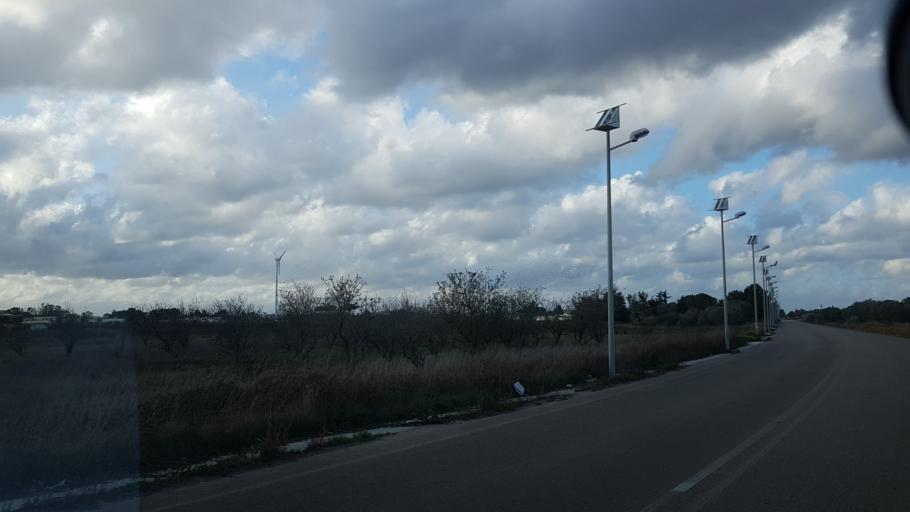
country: IT
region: Apulia
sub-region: Provincia di Brindisi
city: San Pietro Vernotico
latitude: 40.4920
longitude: 18.0099
